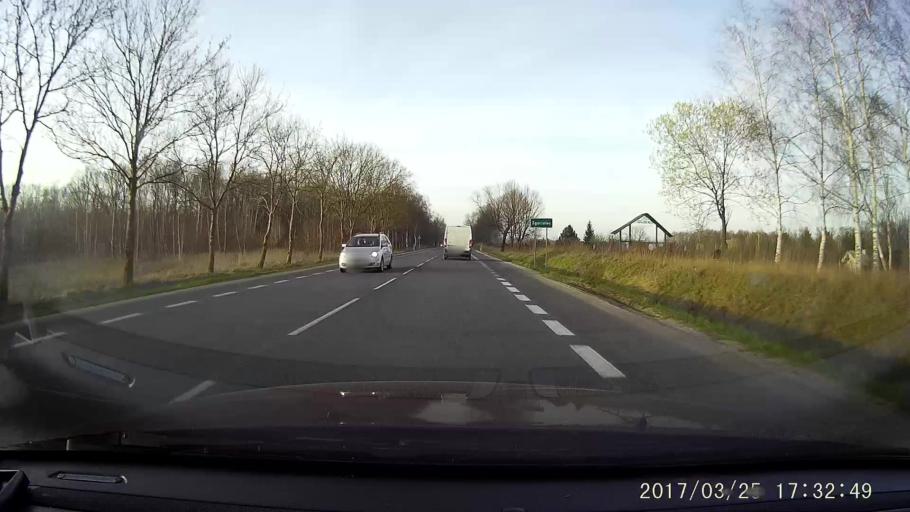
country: PL
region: Lower Silesian Voivodeship
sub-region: Powiat zgorzelecki
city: Zgorzelec
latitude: 51.1202
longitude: 15.0152
